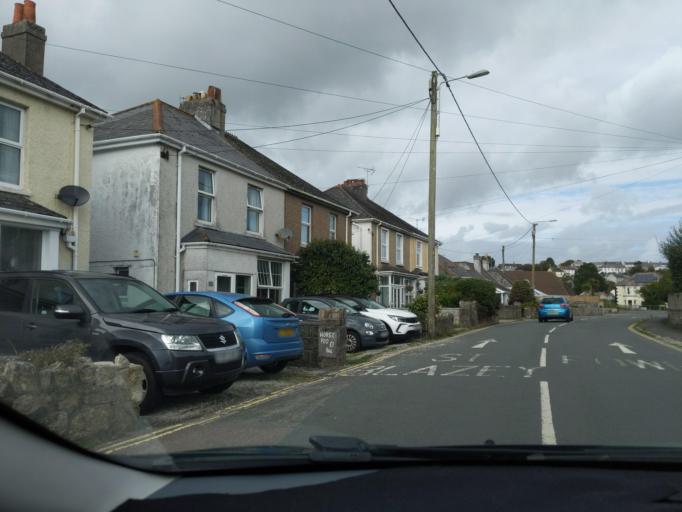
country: GB
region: England
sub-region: Cornwall
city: Par
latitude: 50.3532
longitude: -4.7011
